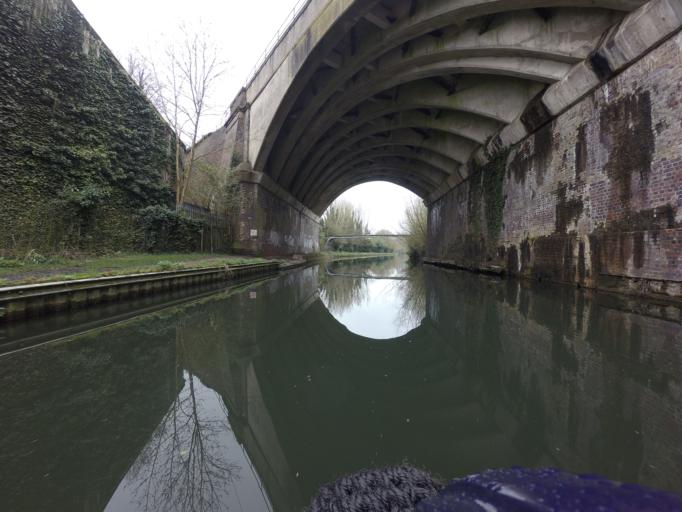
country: GB
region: England
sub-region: Hertfordshire
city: Kings Langley
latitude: 51.7248
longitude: -0.4498
